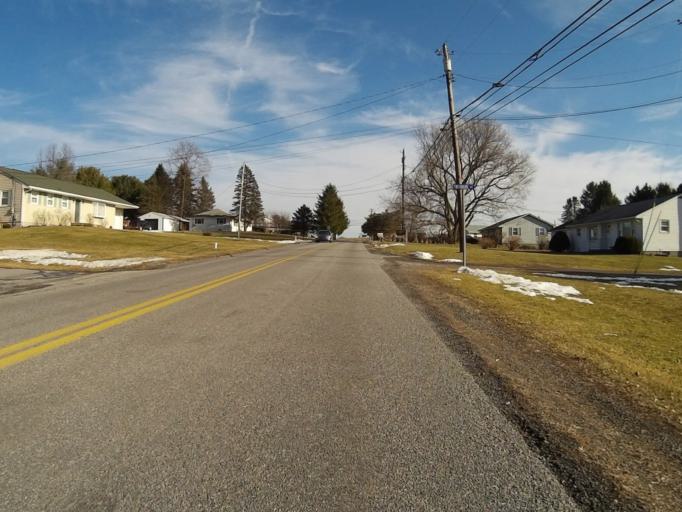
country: US
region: Pennsylvania
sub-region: Centre County
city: Houserville
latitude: 40.8730
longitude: -77.8525
